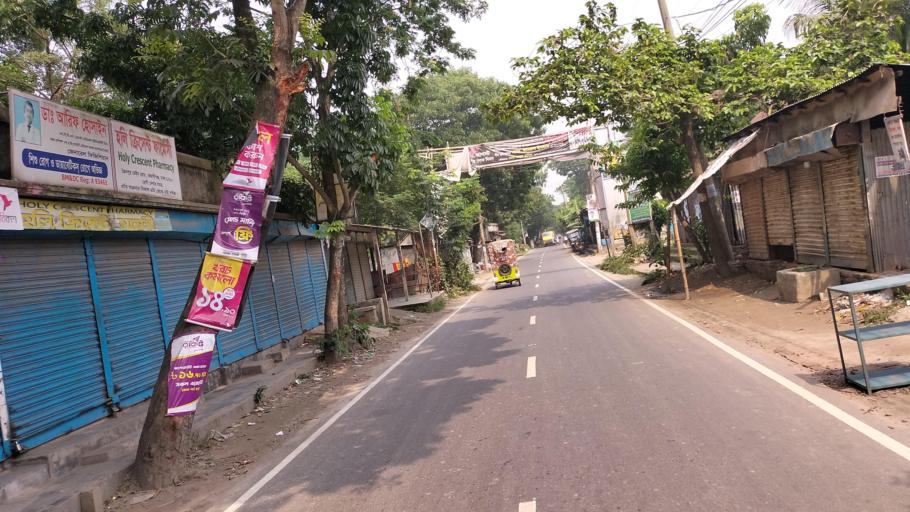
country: BD
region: Dhaka
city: Azimpur
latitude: 23.6975
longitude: 90.2942
